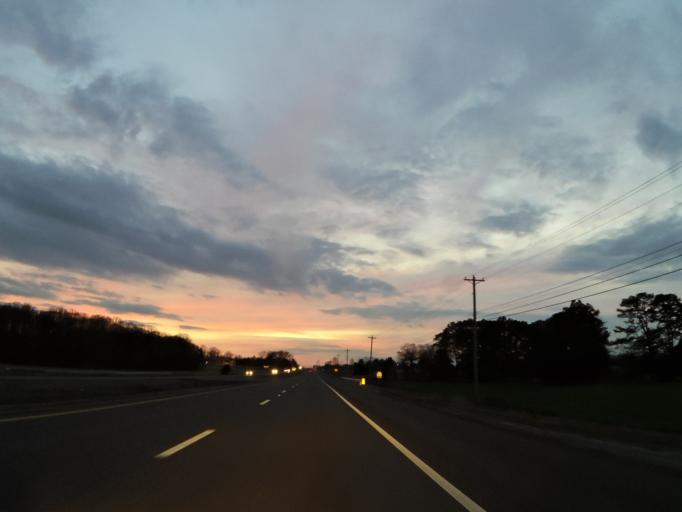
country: US
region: Tennessee
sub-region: Polk County
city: Benton
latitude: 35.1917
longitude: -84.6314
